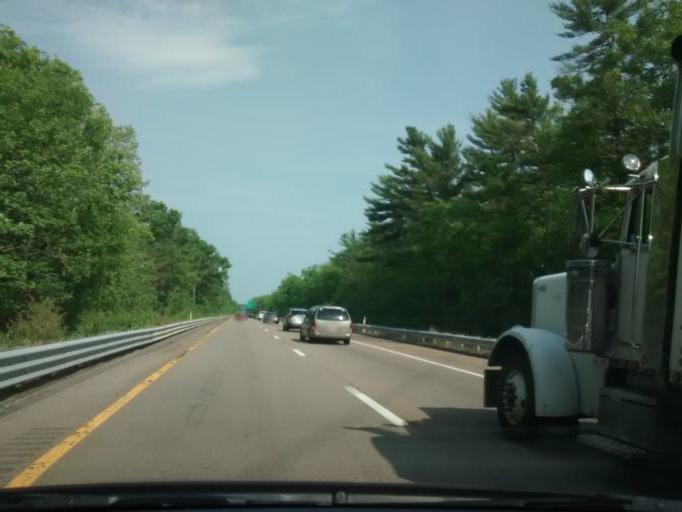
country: US
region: Massachusetts
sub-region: Plymouth County
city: West Wareham
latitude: 41.8118
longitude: -70.7884
